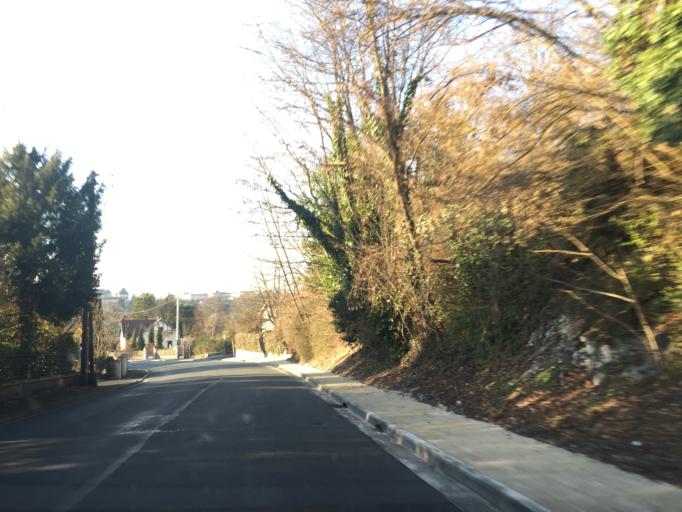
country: FR
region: Poitou-Charentes
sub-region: Departement de la Charente
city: Chalais
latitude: 45.2708
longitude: 0.0493
